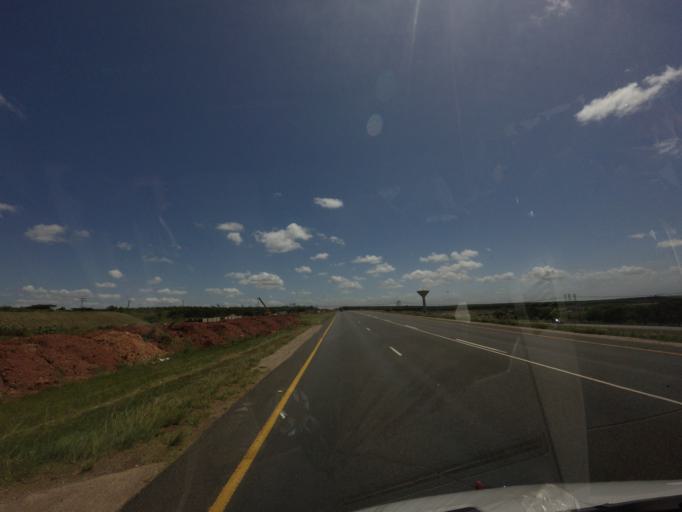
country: ZA
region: KwaZulu-Natal
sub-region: uThungulu District Municipality
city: Empangeni
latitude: -28.7710
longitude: 31.9301
